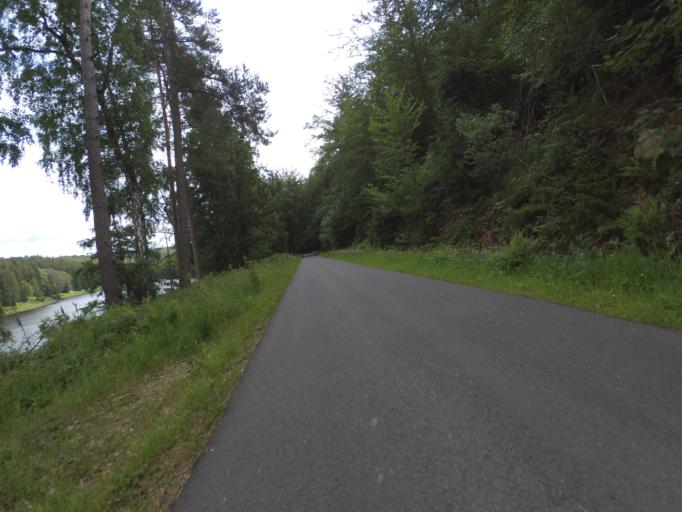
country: BE
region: Wallonia
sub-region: Province de Liege
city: Eupen
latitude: 50.6092
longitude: 6.0929
